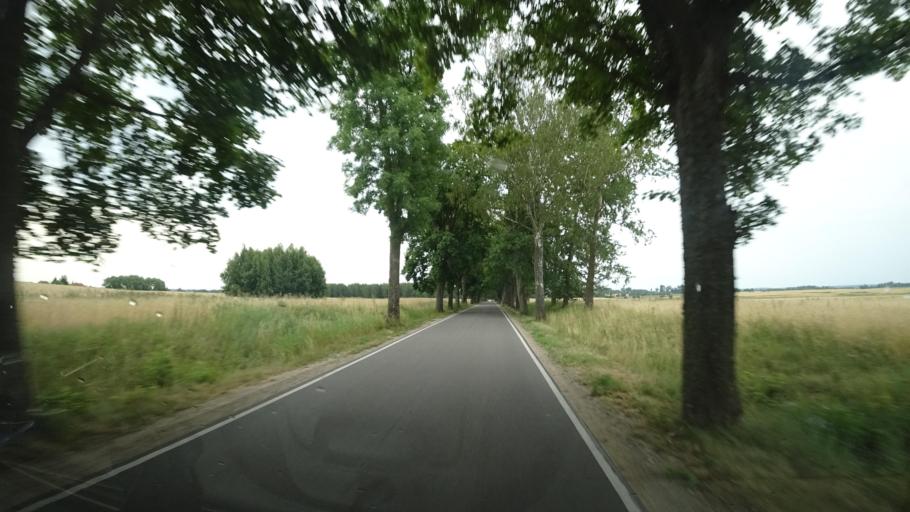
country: PL
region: Warmian-Masurian Voivodeship
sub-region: Powiat mragowski
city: Mikolajki
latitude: 53.8583
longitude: 21.6085
